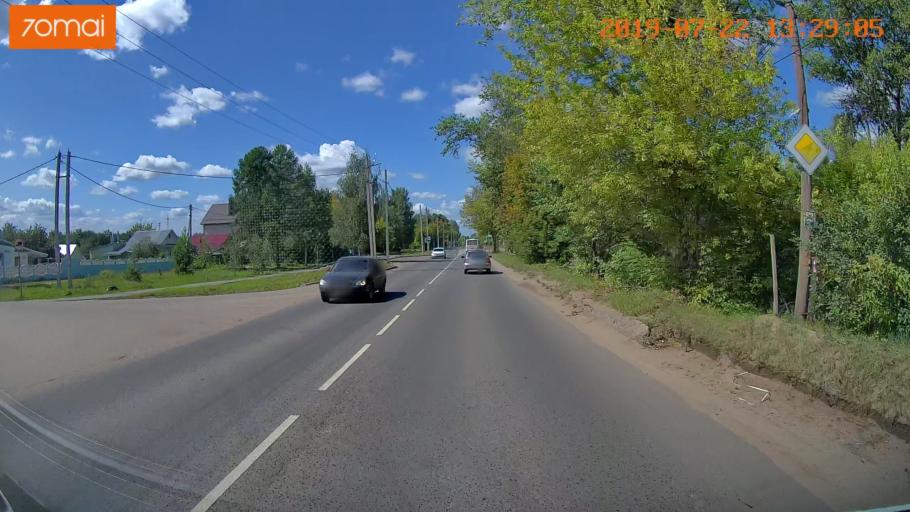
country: RU
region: Ivanovo
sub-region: Gorod Ivanovo
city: Ivanovo
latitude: 57.0453
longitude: 40.9431
